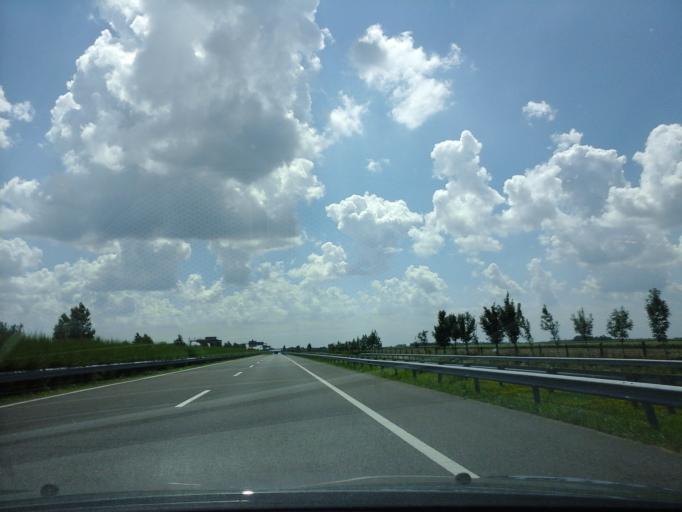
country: HU
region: Hajdu-Bihar
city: Debrecen
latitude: 47.5337
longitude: 21.5517
